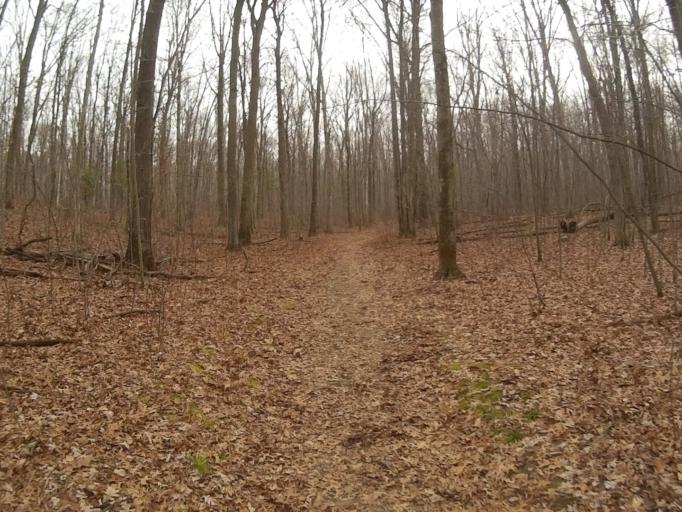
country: US
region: Pennsylvania
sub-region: Centre County
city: Park Forest Village
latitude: 40.7947
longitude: -77.9259
